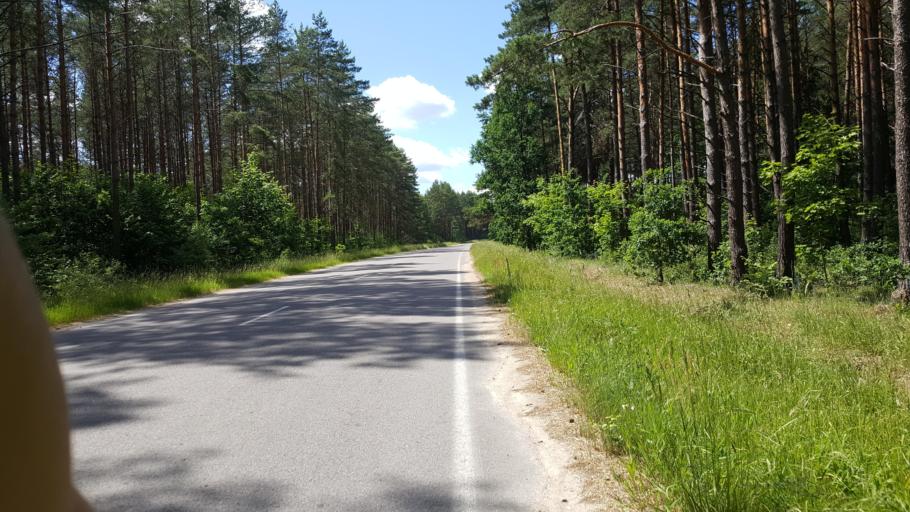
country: PL
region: Podlasie
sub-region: Powiat hajnowski
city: Czeremcha
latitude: 52.5418
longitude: 23.5121
